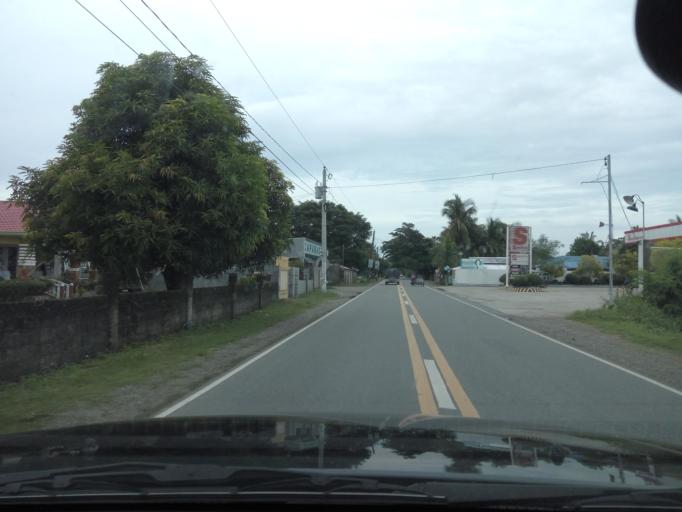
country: PH
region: Central Luzon
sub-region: Province of Nueva Ecija
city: Carmen
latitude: 15.4458
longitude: 120.8299
